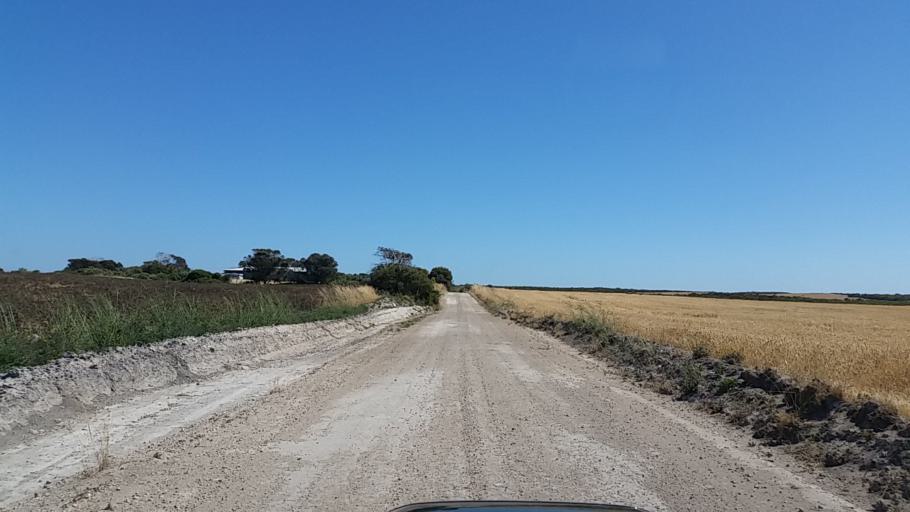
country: AU
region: South Australia
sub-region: Yorke Peninsula
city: Honiton
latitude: -35.2340
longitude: 137.1256
